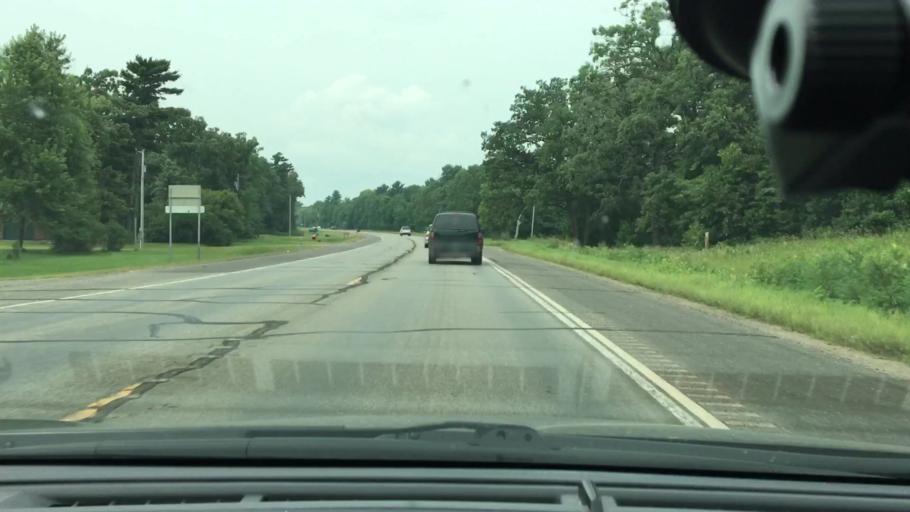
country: US
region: Minnesota
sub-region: Mille Lacs County
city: Vineland
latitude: 46.3267
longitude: -93.7863
